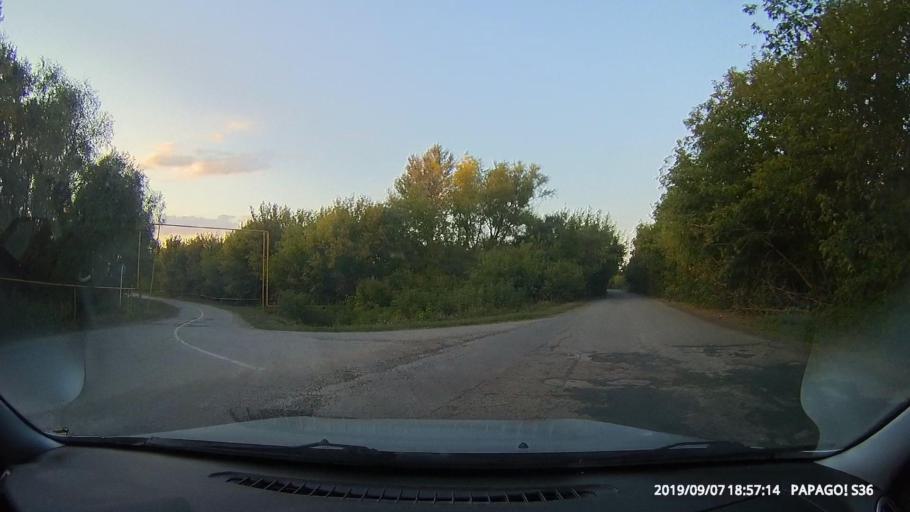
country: RU
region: Samara
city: Chapayevsk
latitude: 52.9929
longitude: 49.7754
